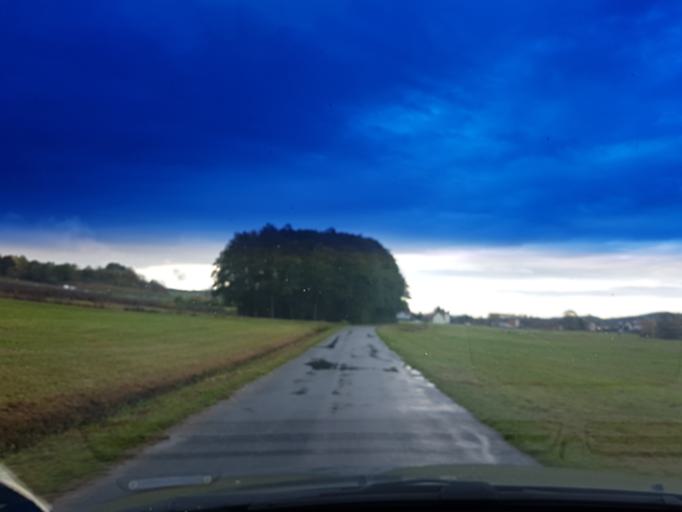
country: DE
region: Bavaria
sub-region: Regierungsbezirk Mittelfranken
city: Burghaslach
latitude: 49.7607
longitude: 10.5798
